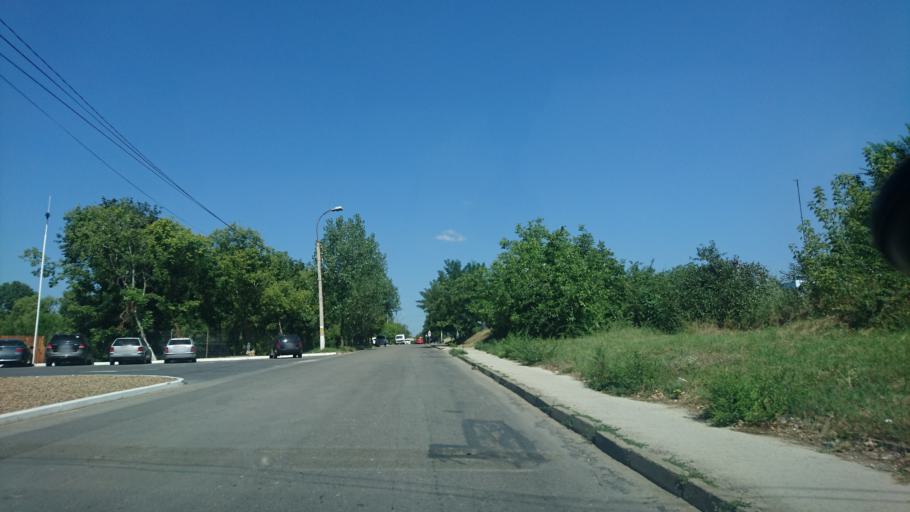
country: MD
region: Laloveni
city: Ialoveni
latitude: 46.9943
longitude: 28.7868
